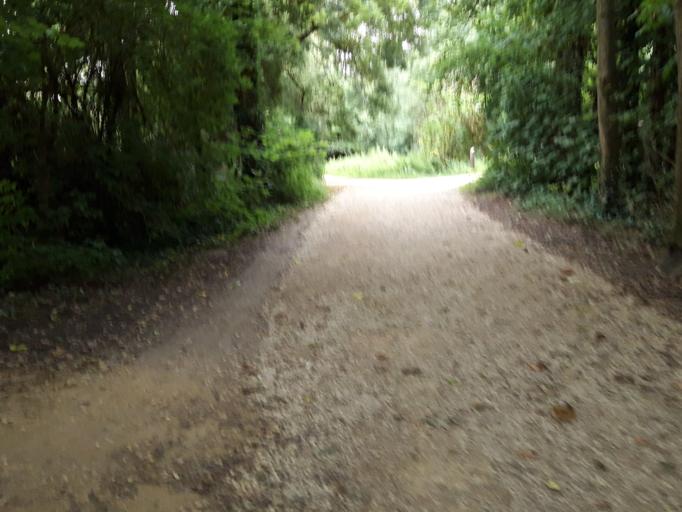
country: FR
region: Ile-de-France
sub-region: Departement de l'Essonne
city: Villemoisson-sur-Orge
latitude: 48.6668
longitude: 2.3334
